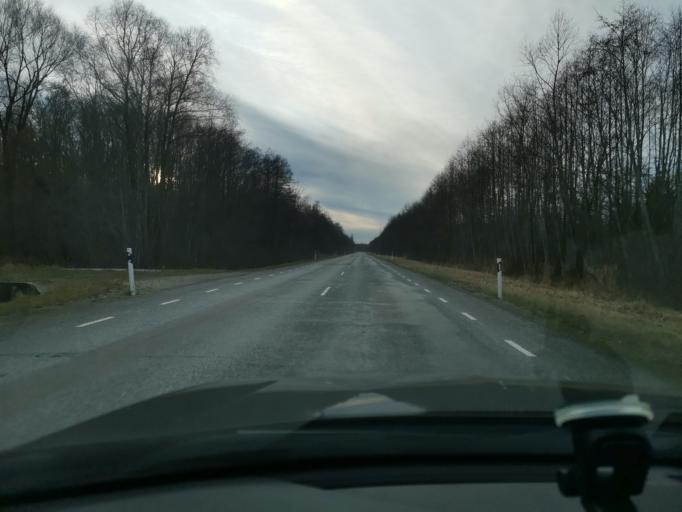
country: EE
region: Ida-Virumaa
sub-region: Narva-Joesuu linn
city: Narva-Joesuu
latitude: 59.3274
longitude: 27.9326
